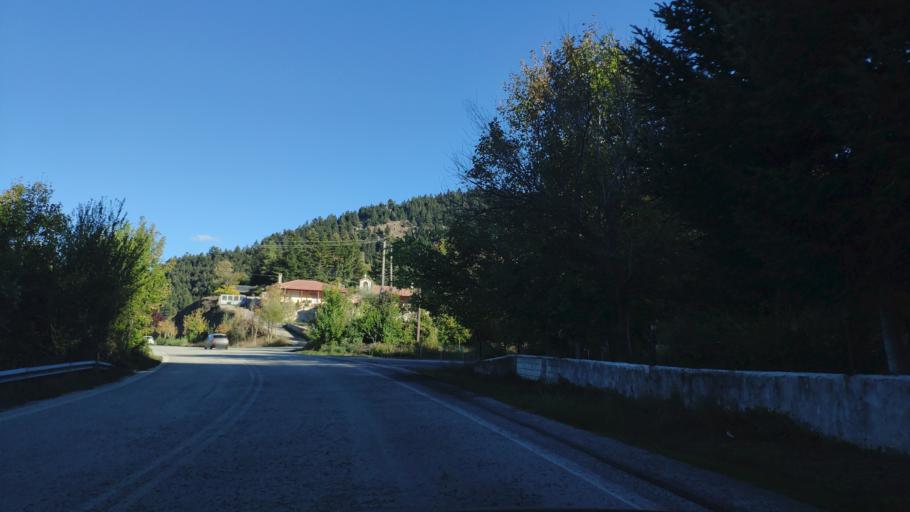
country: GR
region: Peloponnese
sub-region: Nomos Arkadias
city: Langadhia
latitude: 37.6559
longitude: 22.1297
